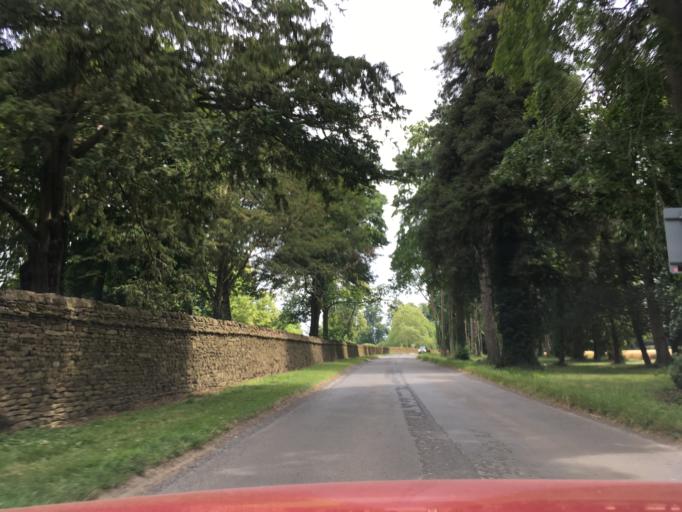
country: GB
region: England
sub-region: Oxfordshire
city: Hook Norton
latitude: 51.9552
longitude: -1.4213
